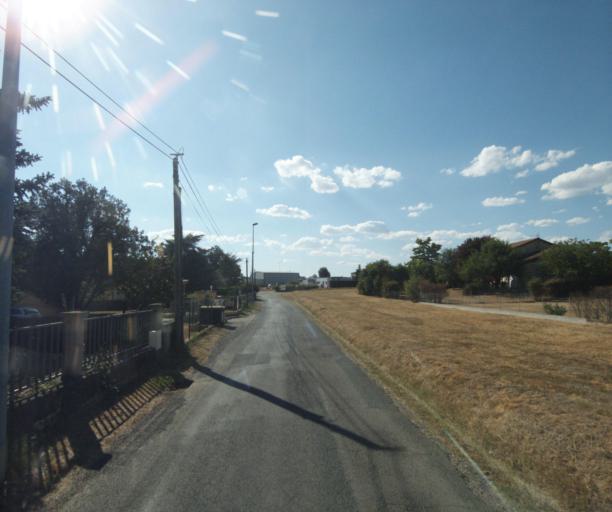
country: FR
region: Rhone-Alpes
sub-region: Departement du Rhone
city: Lentilly
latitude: 45.8164
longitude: 4.6875
